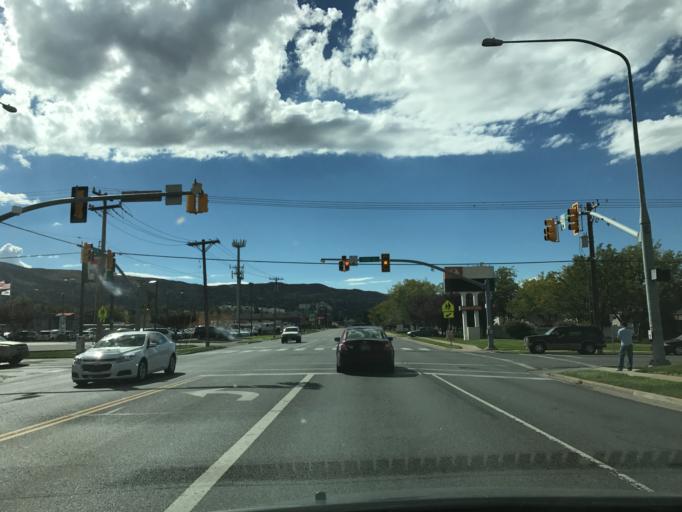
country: US
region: Utah
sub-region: Davis County
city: Woods Cross
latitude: 40.8750
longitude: -111.8923
